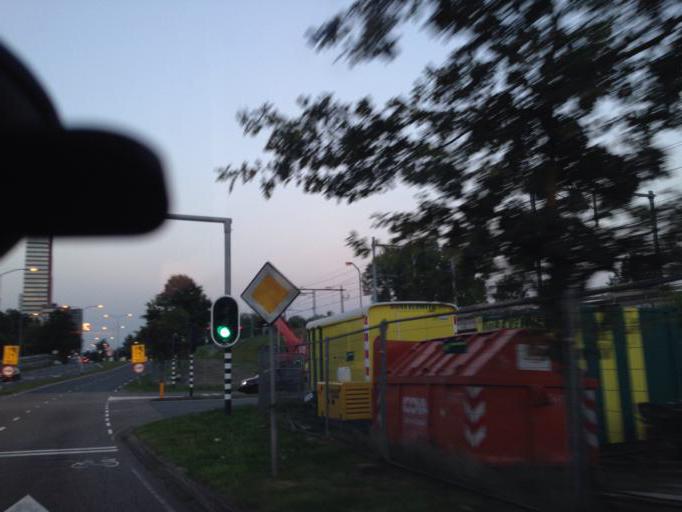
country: NL
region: Flevoland
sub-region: Gemeente Almere
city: Almere Stad
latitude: 52.3740
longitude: 5.2088
